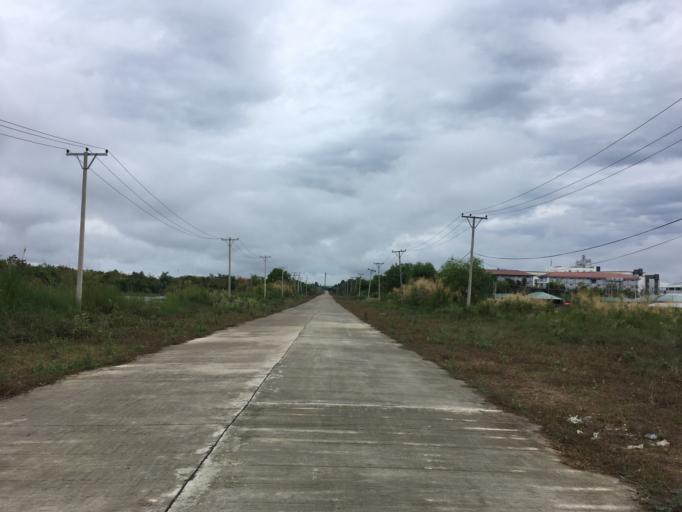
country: MM
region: Mandalay
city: Nay Pyi Taw
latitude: 19.6975
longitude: 96.1201
